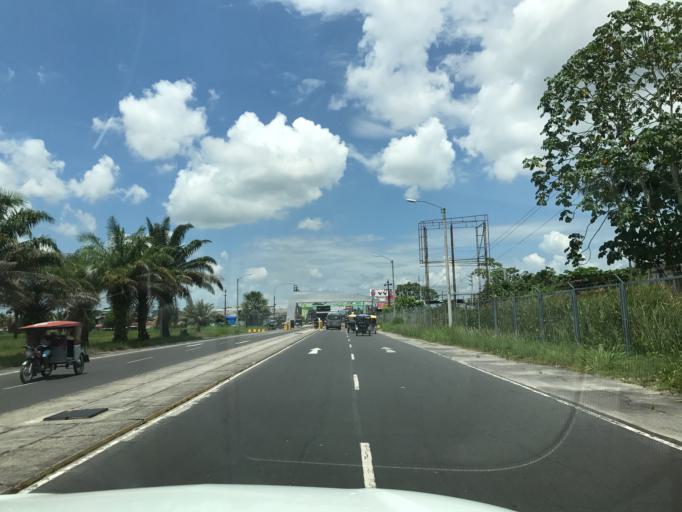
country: PE
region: Loreto
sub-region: Provincia de Maynas
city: Iquitos
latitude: -3.7860
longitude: -73.3009
